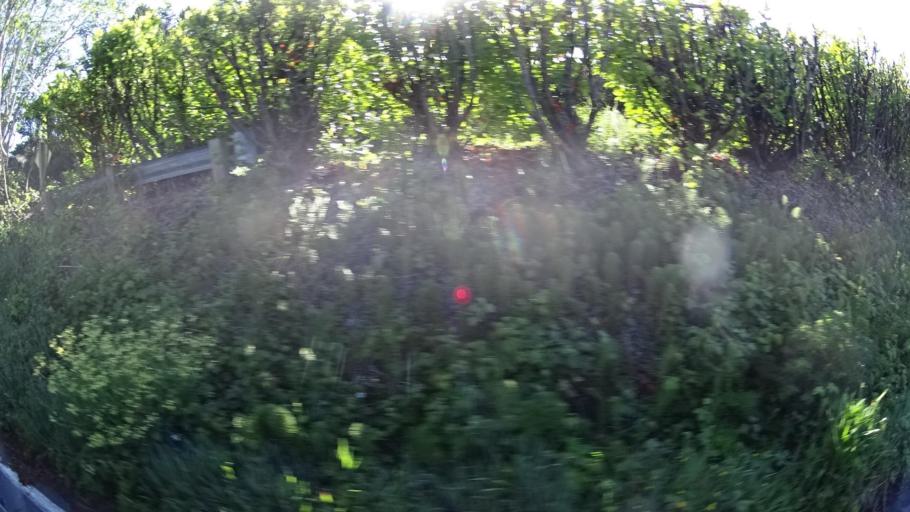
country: US
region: California
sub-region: Humboldt County
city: Westhaven-Moonstone
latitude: 41.1213
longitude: -124.1566
